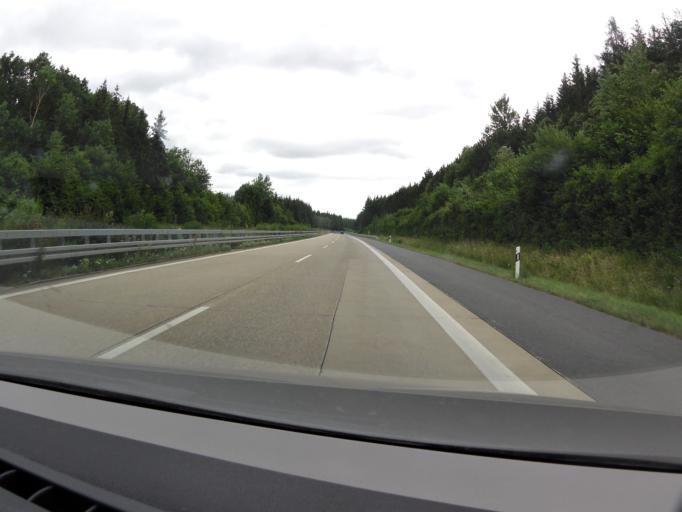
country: DE
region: Baden-Wuerttemberg
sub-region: Karlsruhe Region
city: Rosenberg
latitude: 49.4397
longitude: 9.5137
